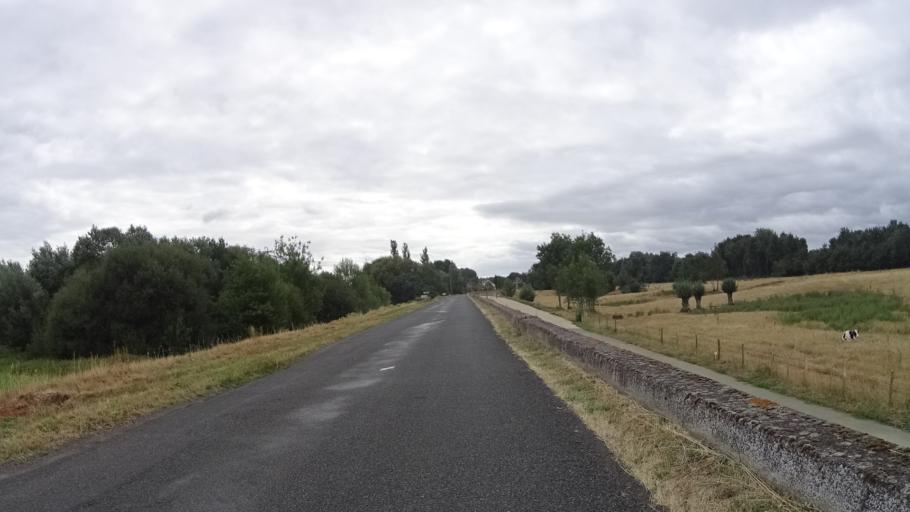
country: FR
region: Pays de la Loire
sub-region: Departement de Maine-et-Loire
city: Chalonnes-sur-Loire
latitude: 47.3698
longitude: -0.7508
